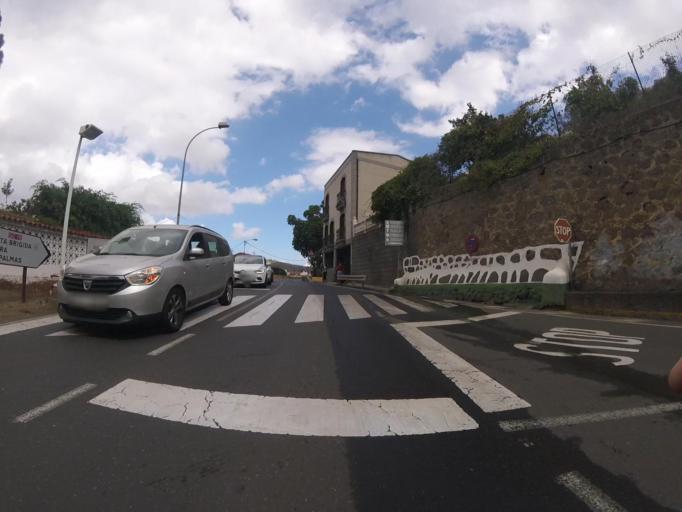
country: ES
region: Canary Islands
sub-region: Provincia de Las Palmas
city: Santa Brigida
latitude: 28.0310
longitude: -15.4997
